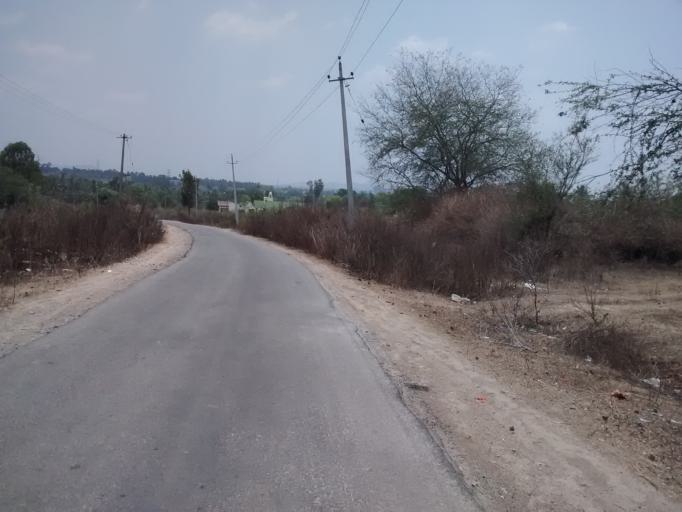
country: IN
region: Karnataka
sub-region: Hassan
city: Hassan
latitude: 12.9469
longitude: 76.1621
